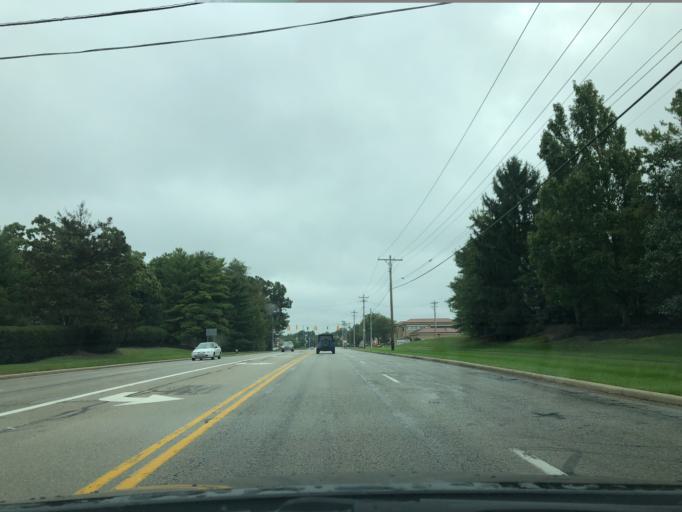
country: US
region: Ohio
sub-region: Hamilton County
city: Sixteen Mile Stand
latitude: 39.2744
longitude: -84.3318
